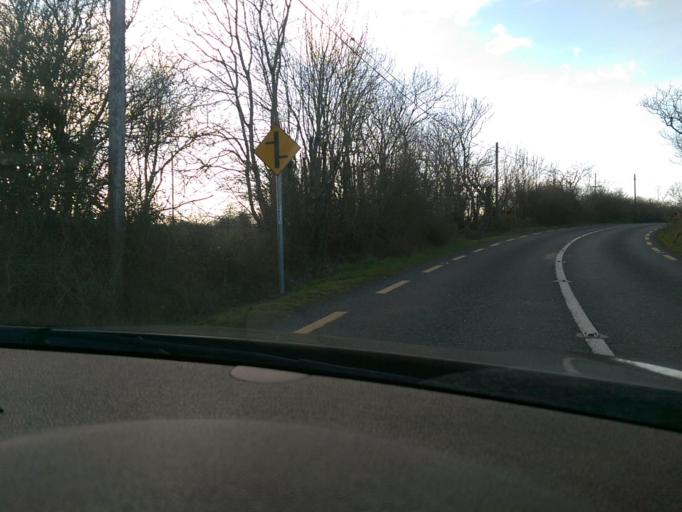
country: IE
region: Connaught
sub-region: Roscommon
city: Boyle
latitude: 53.9216
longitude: -8.2771
